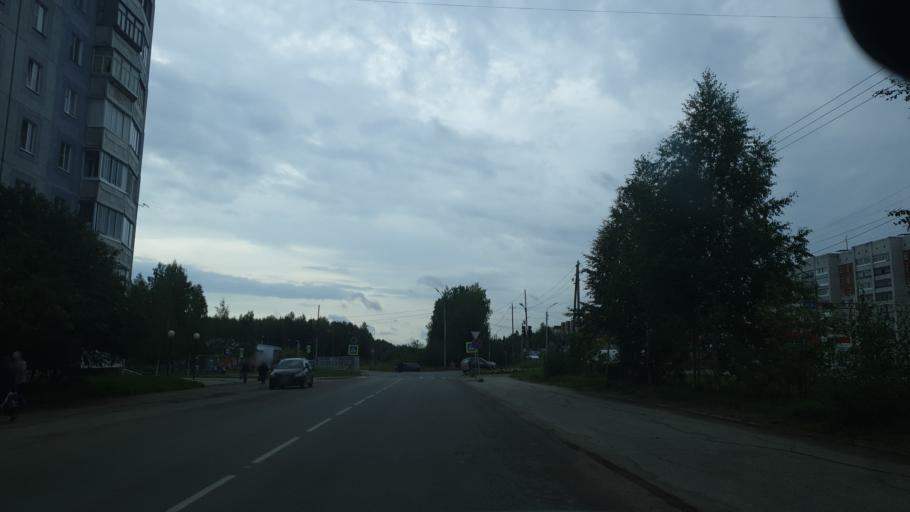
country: RU
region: Komi Republic
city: Ezhva
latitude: 61.7822
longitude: 50.7480
